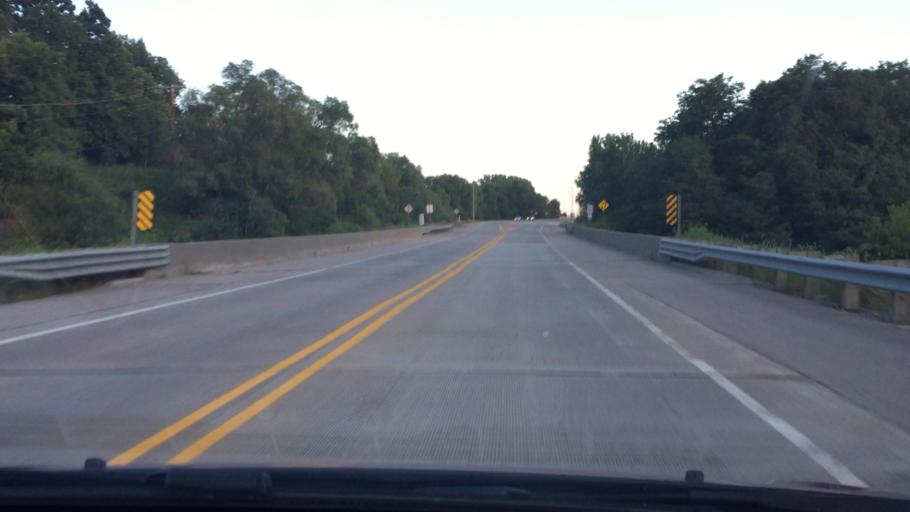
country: US
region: Iowa
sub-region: Muscatine County
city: Muscatine
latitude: 41.4604
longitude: -91.0317
